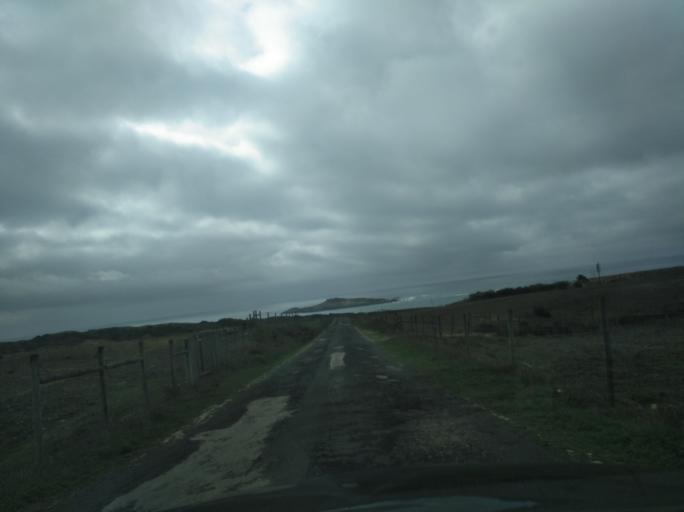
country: PT
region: Setubal
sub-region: Sines
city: Porto Covo
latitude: 37.8398
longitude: -8.7845
